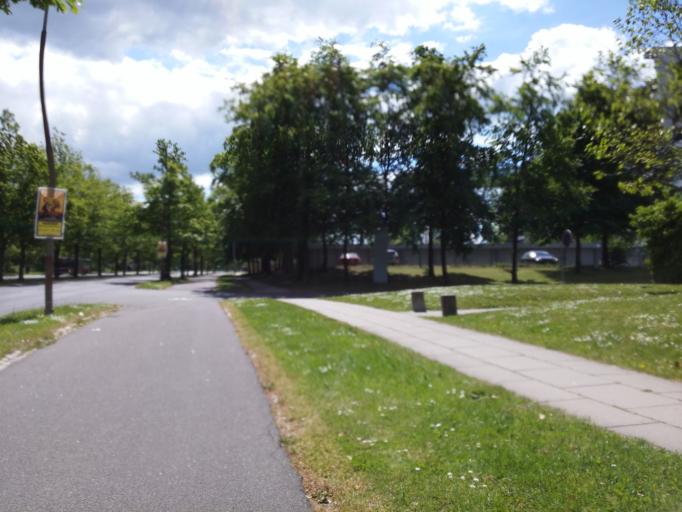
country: DK
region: South Denmark
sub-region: Odense Kommune
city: Seden
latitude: 55.4113
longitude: 10.4414
